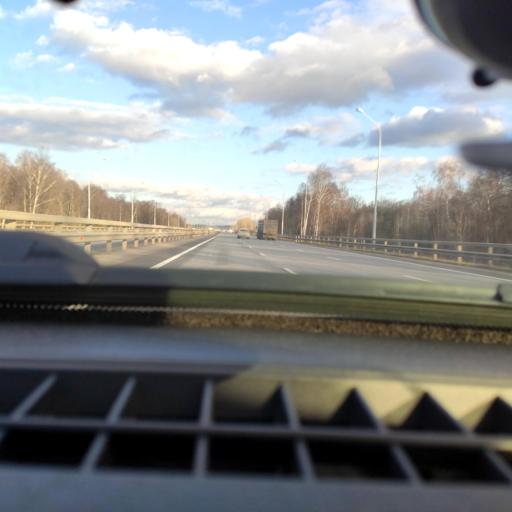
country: RU
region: Bashkortostan
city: Ufa
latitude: 54.6490
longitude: 56.0455
